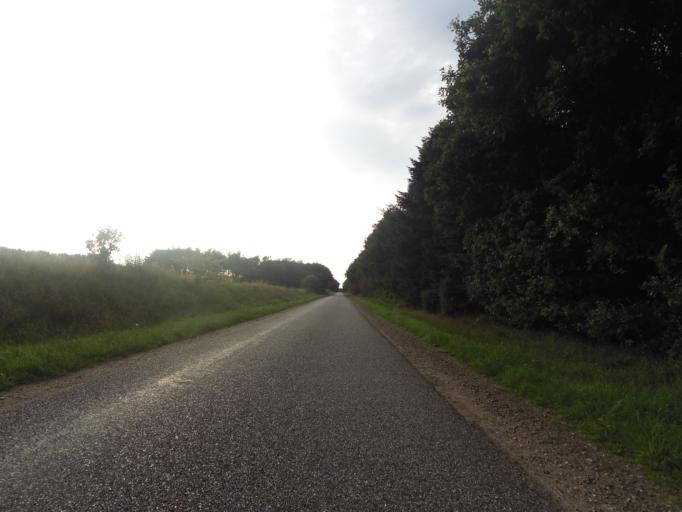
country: DK
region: South Denmark
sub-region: Tonder Kommune
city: Logumkloster
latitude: 55.1522
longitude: 8.9471
